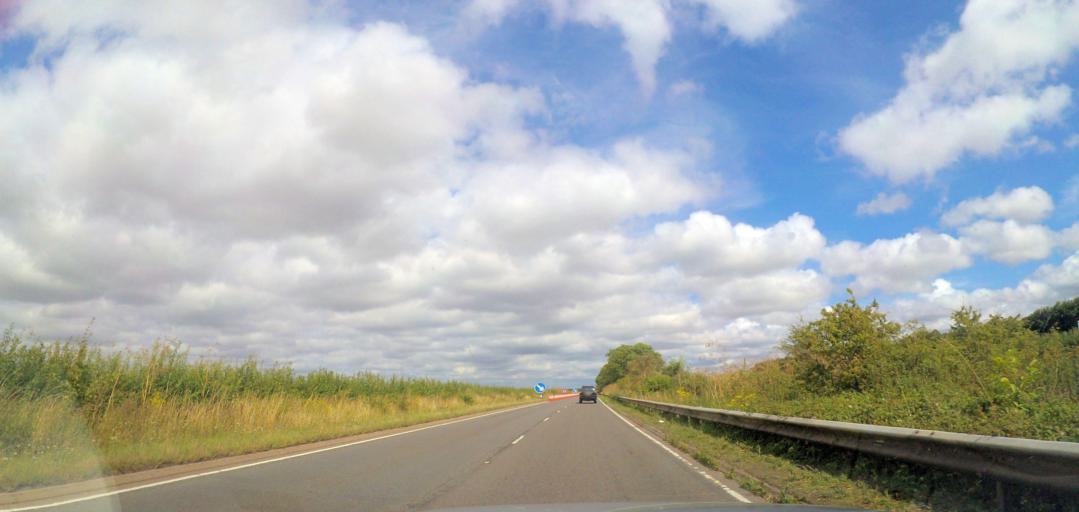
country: GB
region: England
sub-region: Cambridgeshire
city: Bassingbourn
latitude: 52.0394
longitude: -0.0752
